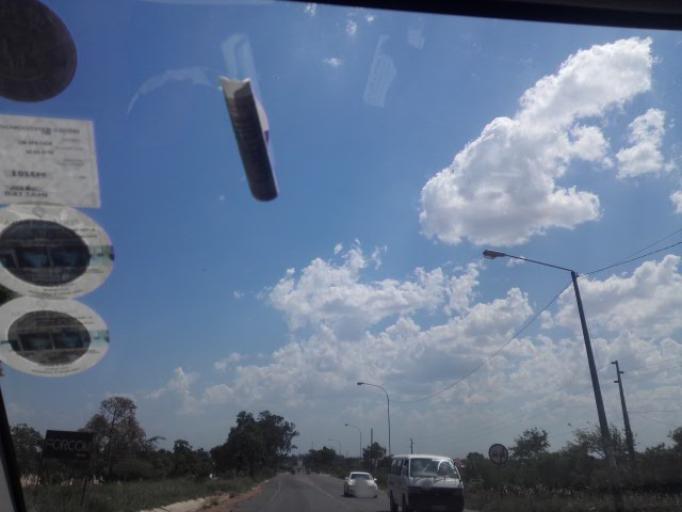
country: MZ
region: Maputo
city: Matola
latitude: -25.9657
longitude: 32.4454
